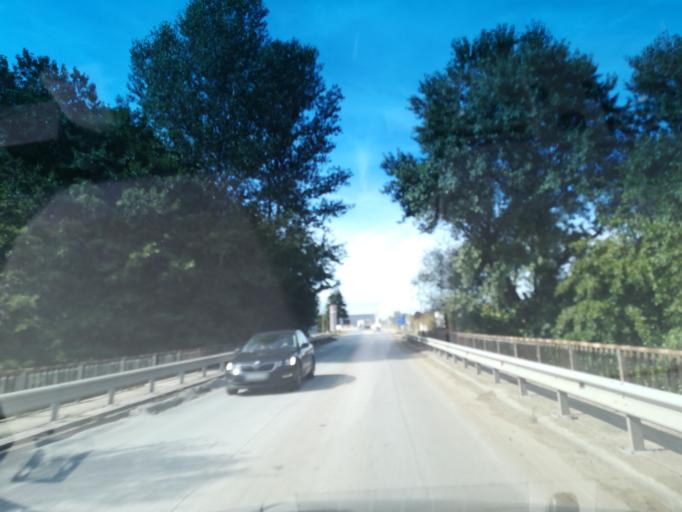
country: BG
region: Plovdiv
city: Stamboliyski
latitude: 42.1197
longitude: 24.5558
